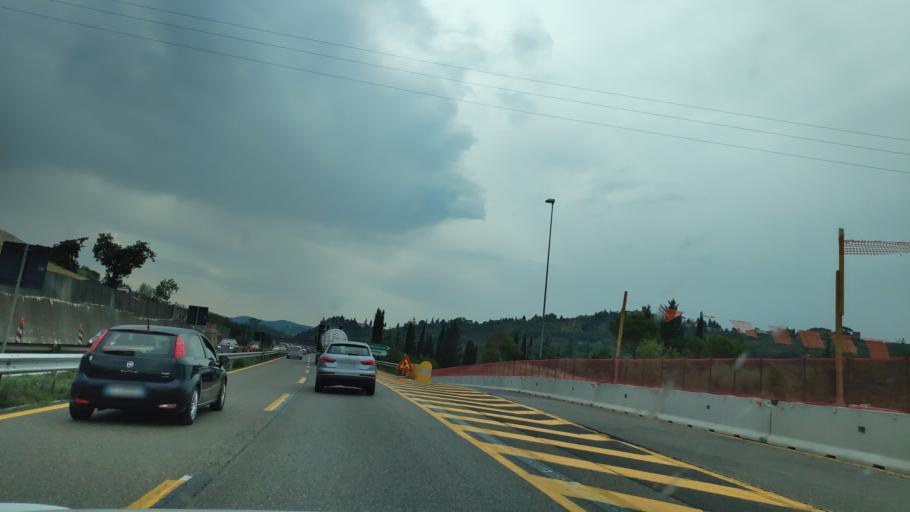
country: IT
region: Tuscany
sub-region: Province of Florence
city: Grassina Ponte a Ema
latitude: 43.7407
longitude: 11.2821
